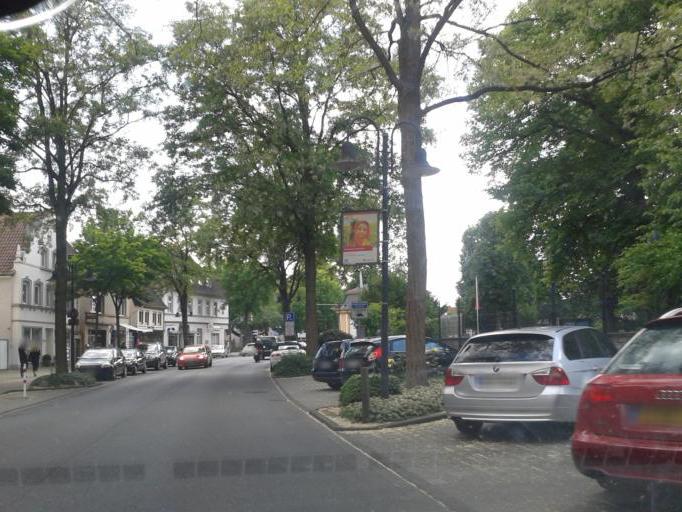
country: DE
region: North Rhine-Westphalia
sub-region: Regierungsbezirk Detmold
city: Paderborn
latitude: 51.7456
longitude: 8.7142
